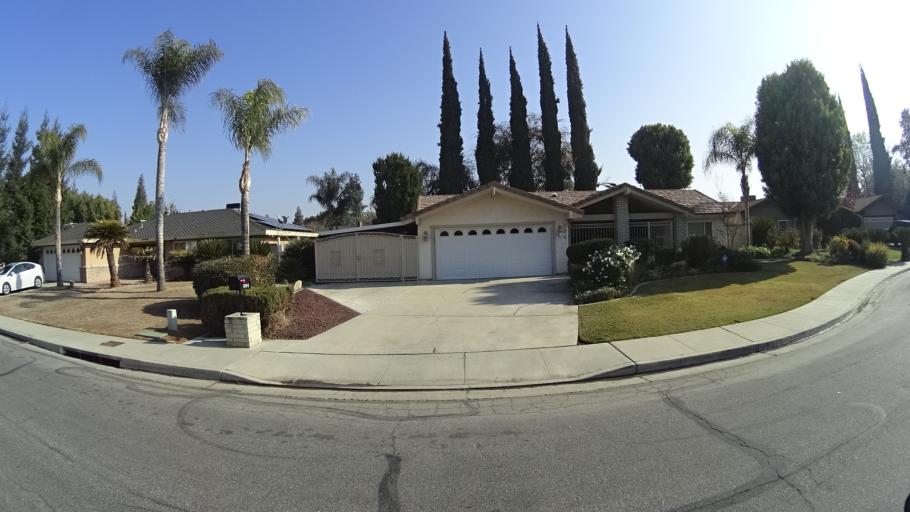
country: US
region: California
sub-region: Kern County
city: Greenacres
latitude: 35.3568
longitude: -119.0750
